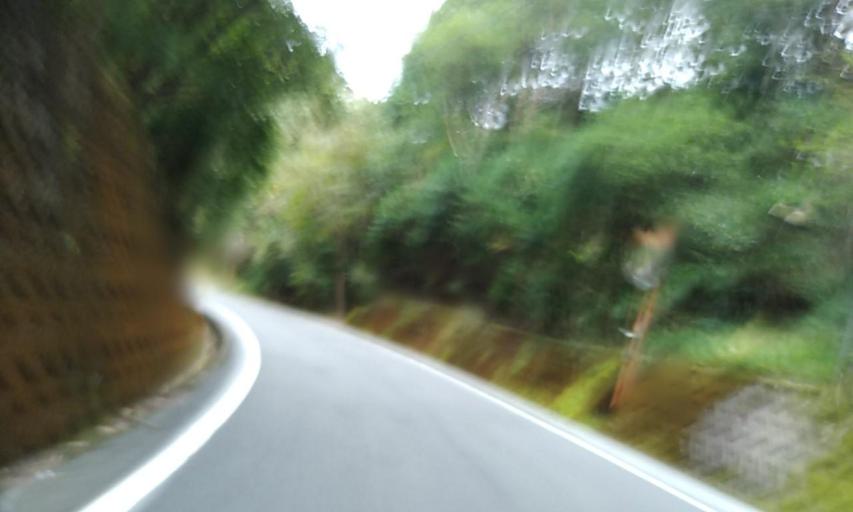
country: JP
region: Wakayama
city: Shingu
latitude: 33.5401
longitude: 135.8372
